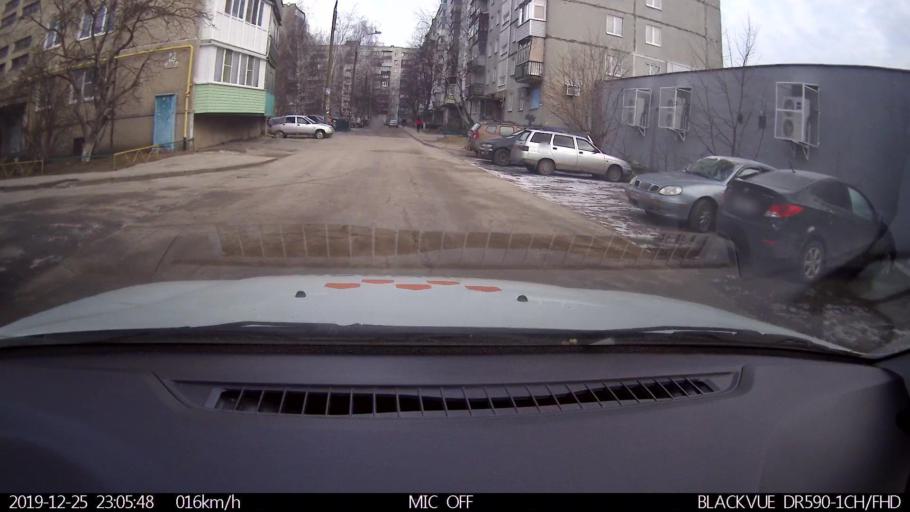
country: RU
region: Nizjnij Novgorod
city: Gorbatovka
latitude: 56.3613
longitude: 43.8061
